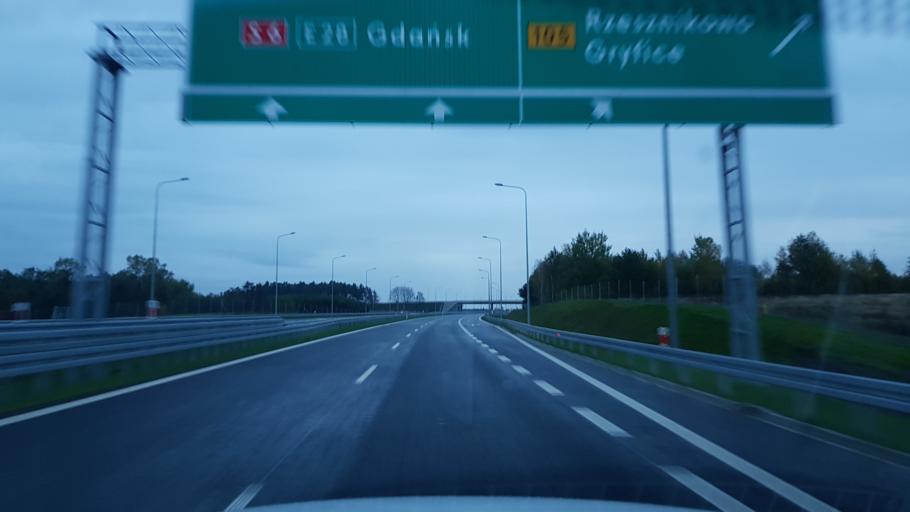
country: PL
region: West Pomeranian Voivodeship
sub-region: Powiat gryficki
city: Brojce
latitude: 53.9393
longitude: 15.3953
